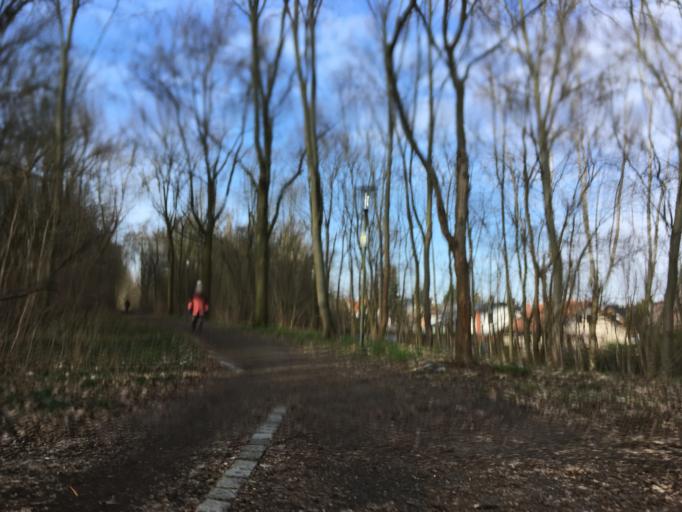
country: DE
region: Berlin
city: Rosenthal
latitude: 52.6104
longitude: 13.3728
